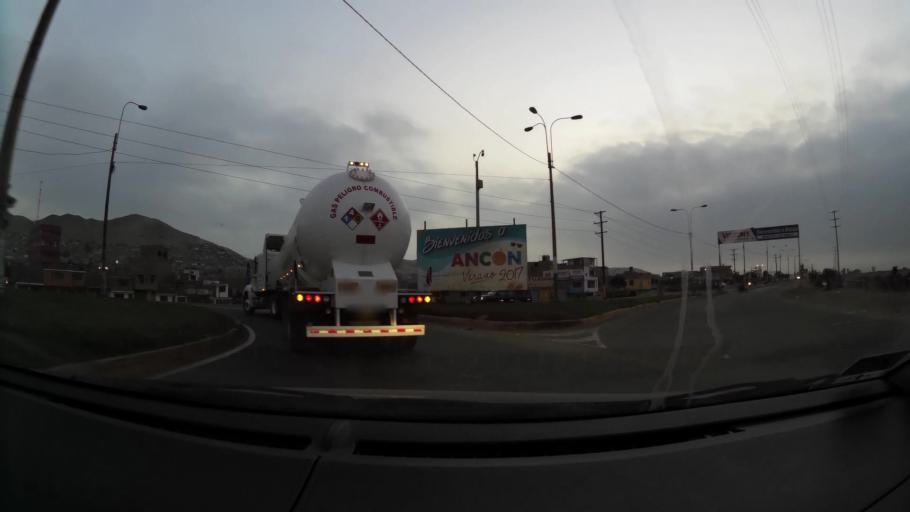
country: PE
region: Lima
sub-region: Lima
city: Santa Rosa
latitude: -11.7754
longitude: -77.1644
